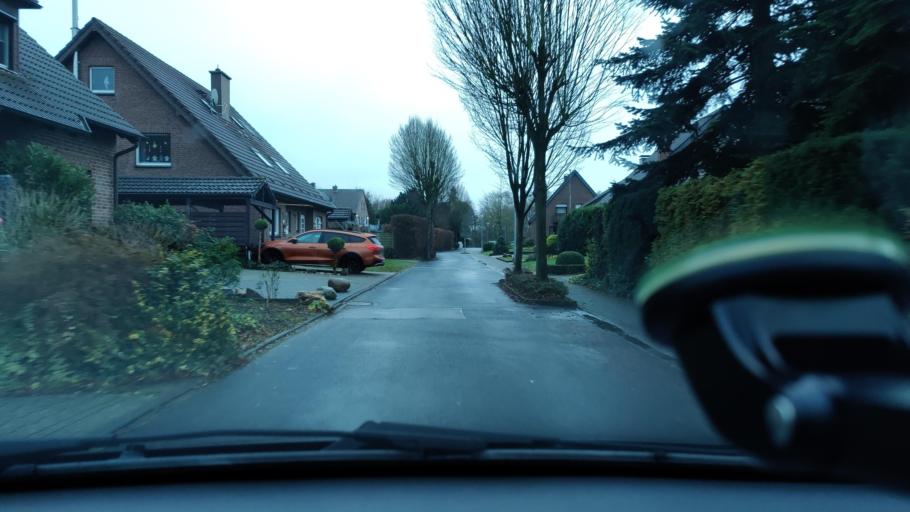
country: DE
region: North Rhine-Westphalia
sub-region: Regierungsbezirk Dusseldorf
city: Xanten
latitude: 51.6697
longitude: 6.4661
